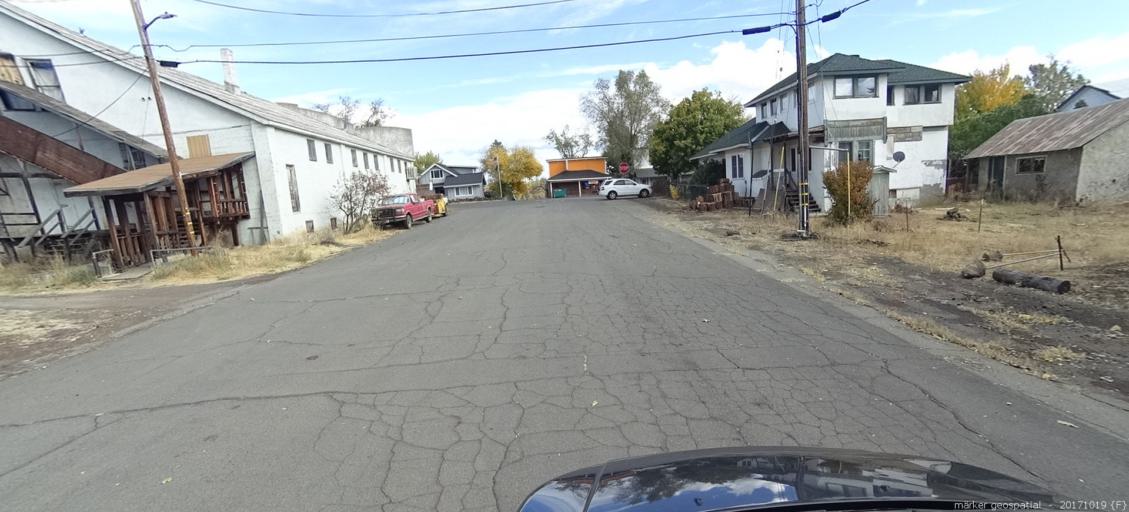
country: US
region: California
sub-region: Shasta County
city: Burney
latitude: 41.0050
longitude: -121.4387
